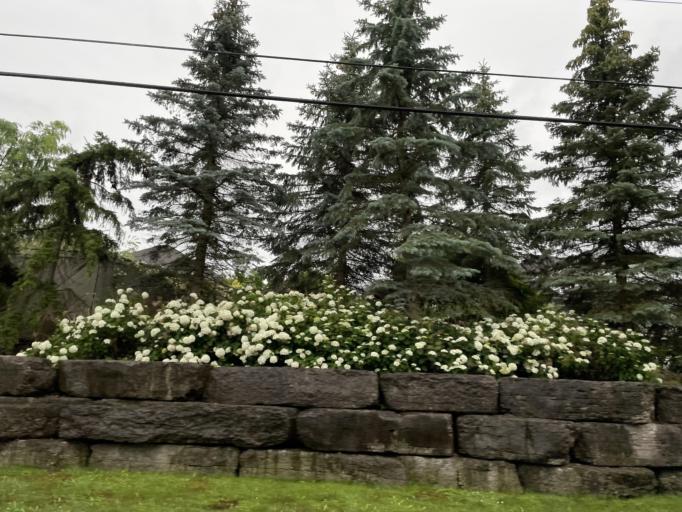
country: CA
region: Ontario
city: Cambridge
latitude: 43.4230
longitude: -80.2705
